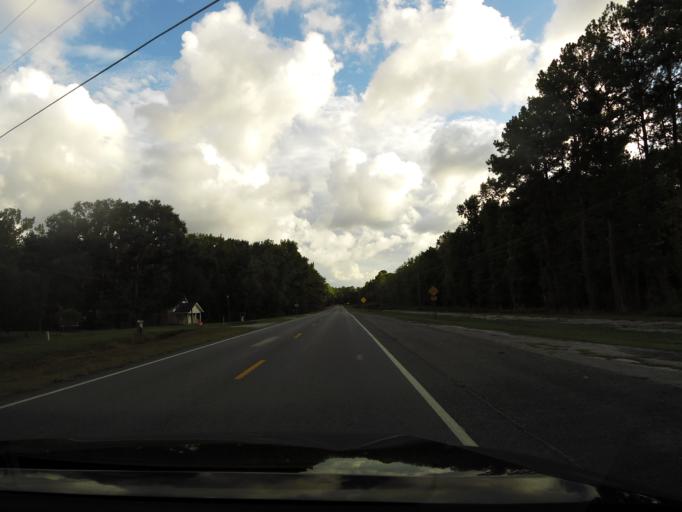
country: US
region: Georgia
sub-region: Liberty County
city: Midway
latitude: 31.7147
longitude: -81.4167
